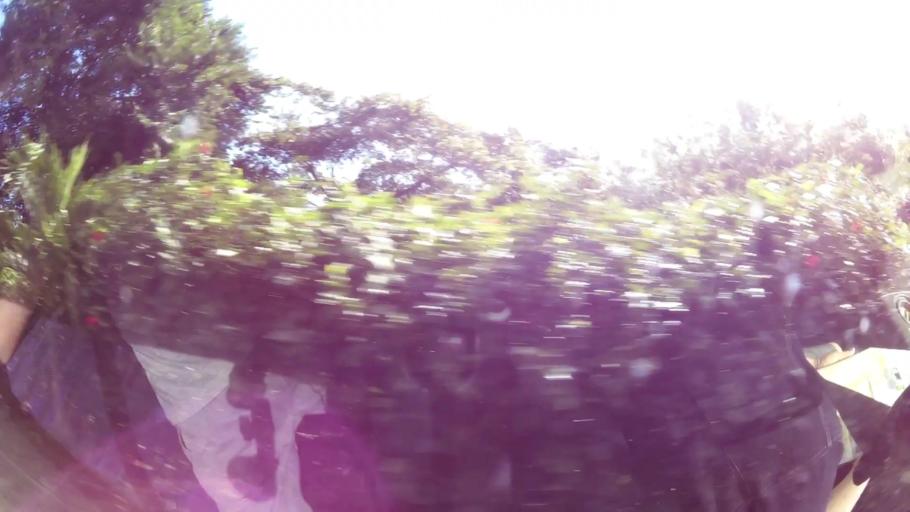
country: DM
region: Saint Andrew
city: Marigot
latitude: 15.5163
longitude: -61.2713
